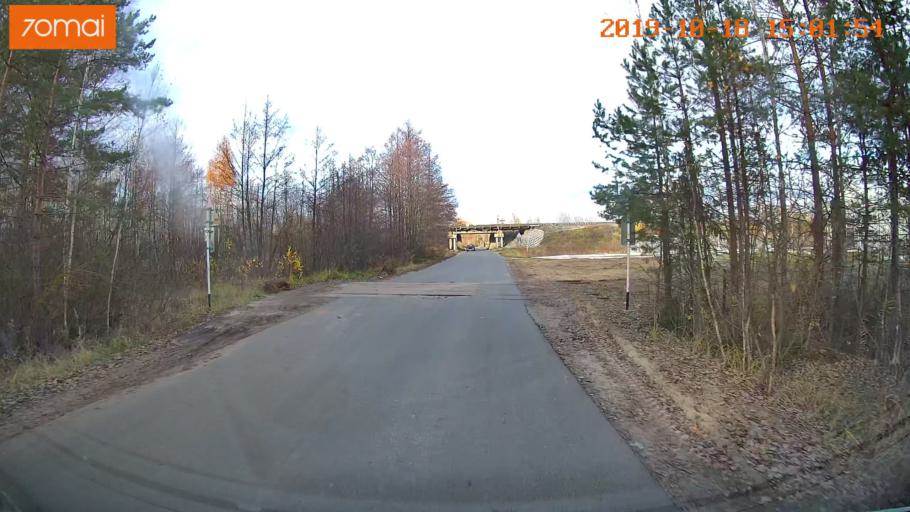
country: RU
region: Vladimir
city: Gus'-Khrustal'nyy
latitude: 55.5011
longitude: 40.6084
